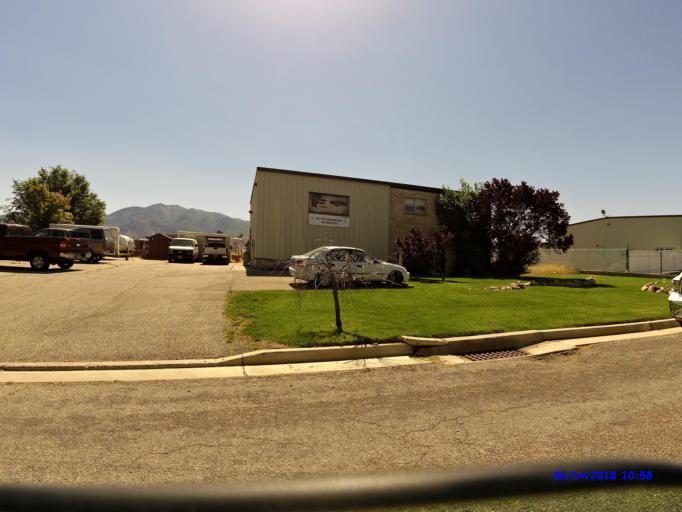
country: US
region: Utah
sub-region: Weber County
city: Riverdale
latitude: 41.2033
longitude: -112.0166
